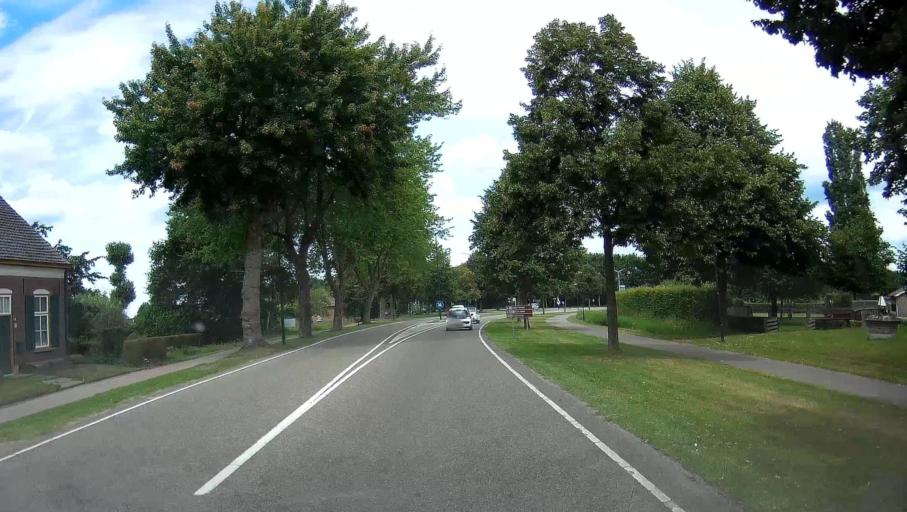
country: NL
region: North Brabant
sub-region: Gemeente Hilvarenbeek
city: Hilvarenbeek
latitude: 51.5002
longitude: 5.1304
